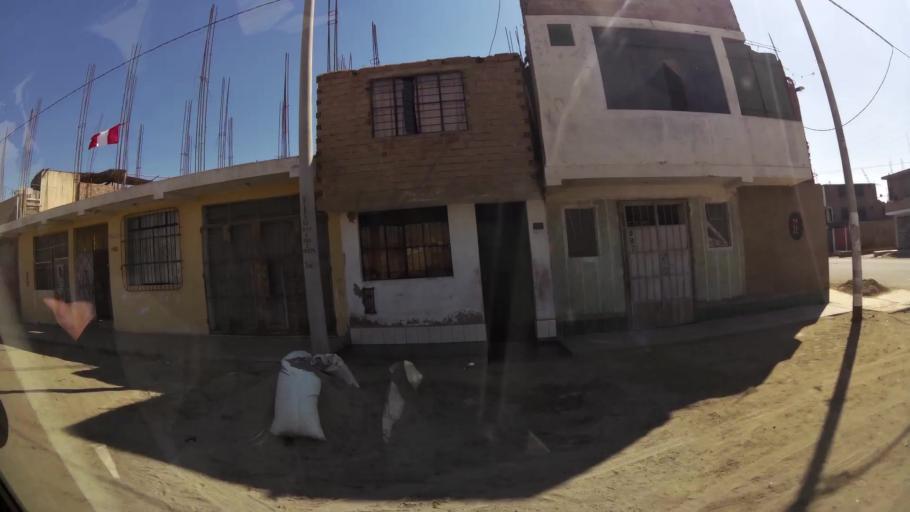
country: PE
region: Ica
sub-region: Provincia de Ica
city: La Tinguina
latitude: -14.0325
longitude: -75.7074
